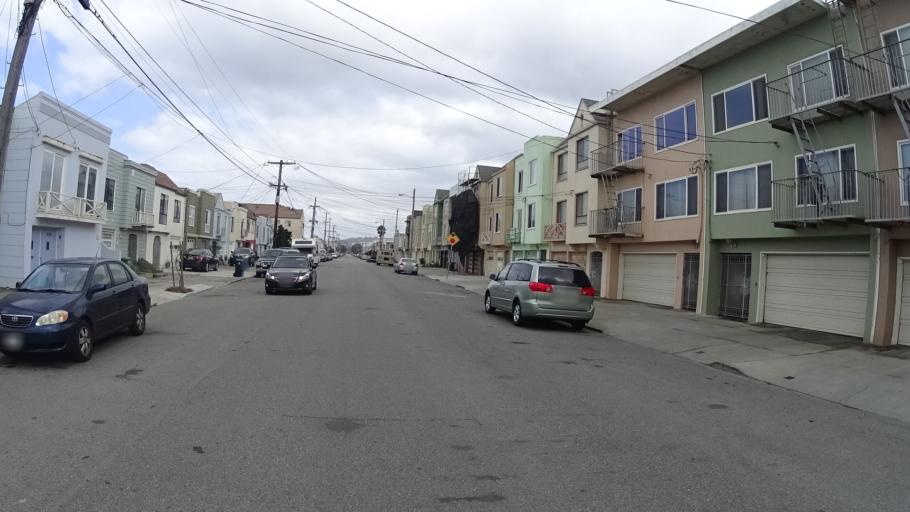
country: US
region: California
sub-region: San Mateo County
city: Daly City
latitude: 37.7516
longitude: -122.5075
